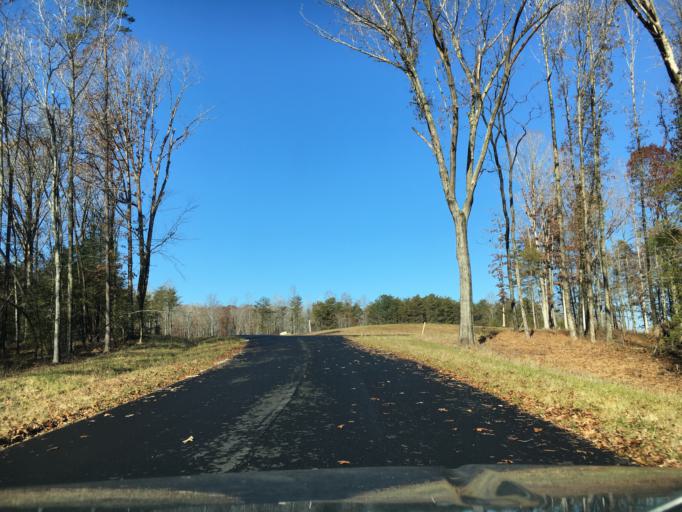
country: US
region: Virginia
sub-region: Goochland County
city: Goochland
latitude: 37.6921
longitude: -77.8395
